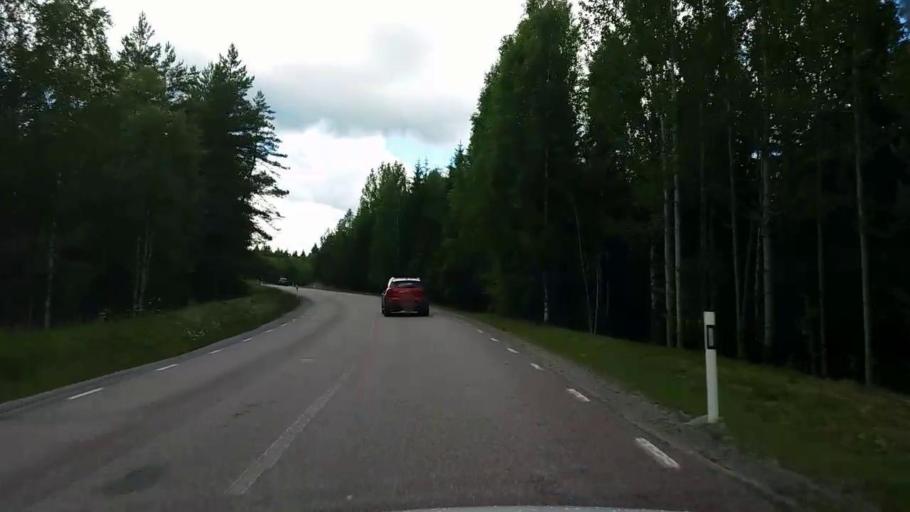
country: SE
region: Vaestmanland
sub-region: Fagersta Kommun
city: Fagersta
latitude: 59.8824
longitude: 15.8364
